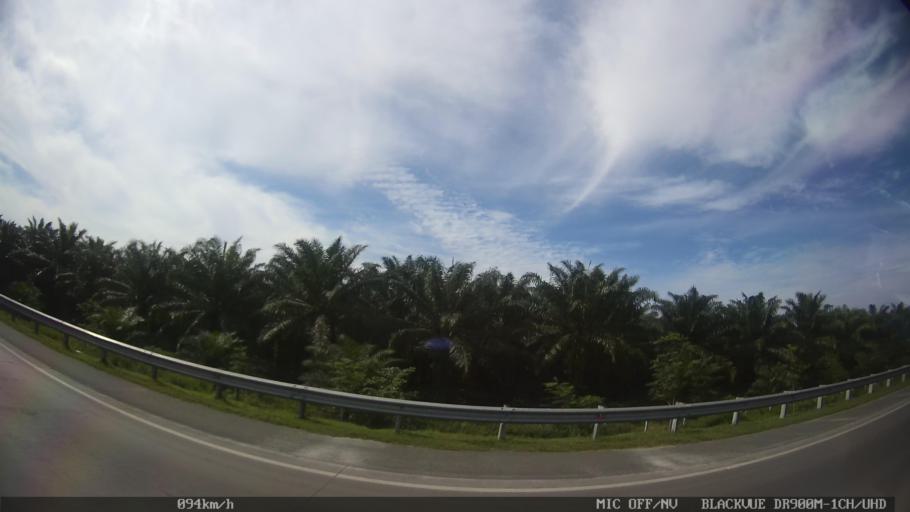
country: ID
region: North Sumatra
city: Sunggal
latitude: 3.6382
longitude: 98.6052
